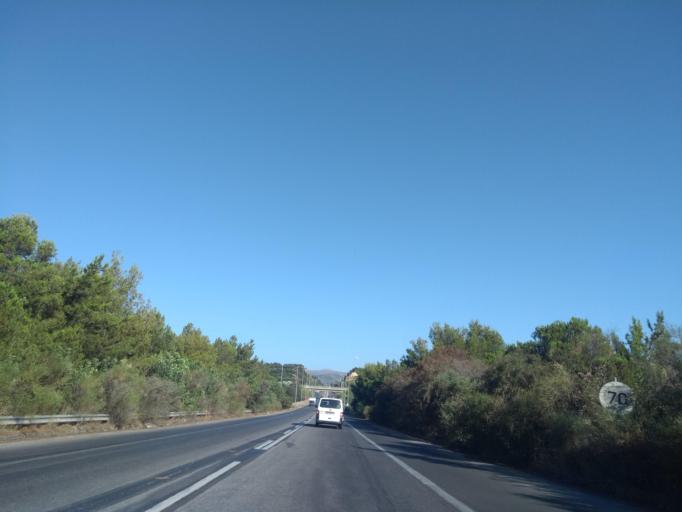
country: GR
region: Crete
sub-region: Nomos Chanias
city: Gerani
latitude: 35.5176
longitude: 23.8235
